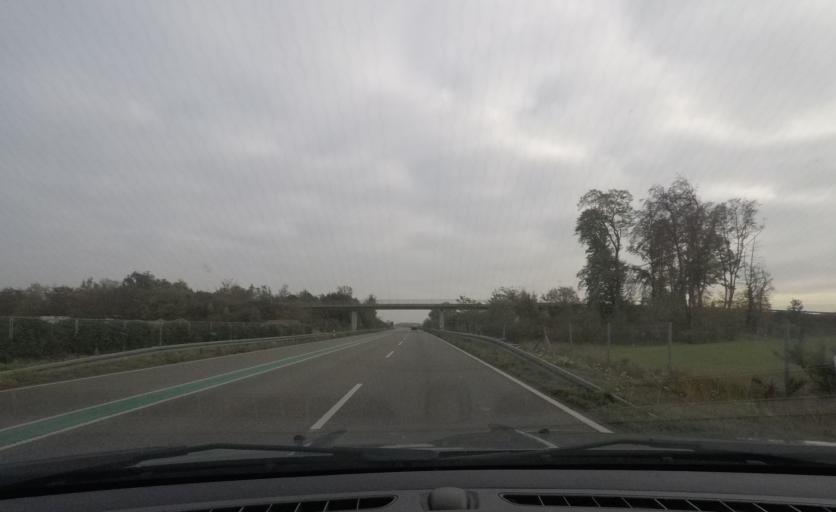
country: DE
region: North Rhine-Westphalia
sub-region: Regierungsbezirk Munster
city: Rhede
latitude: 51.8247
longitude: 6.7198
